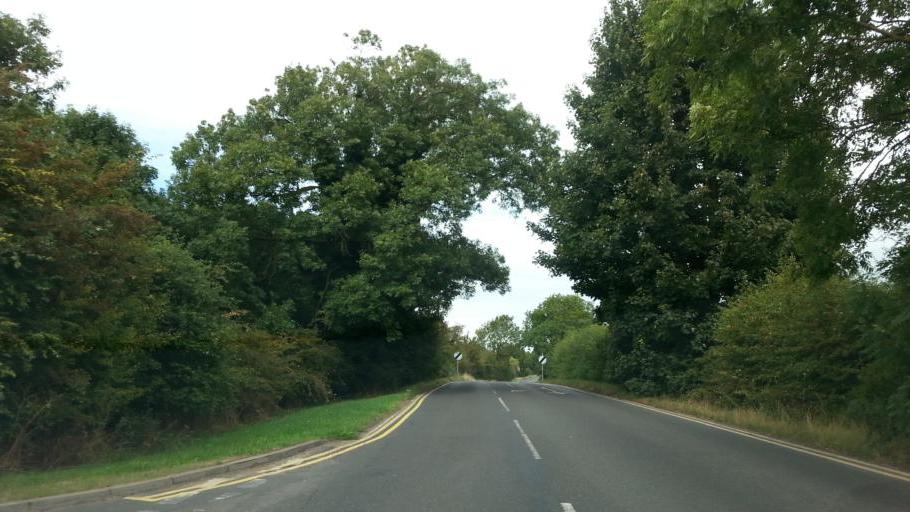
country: GB
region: England
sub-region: Cambridgeshire
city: Sawston
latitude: 52.1690
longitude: 0.1629
